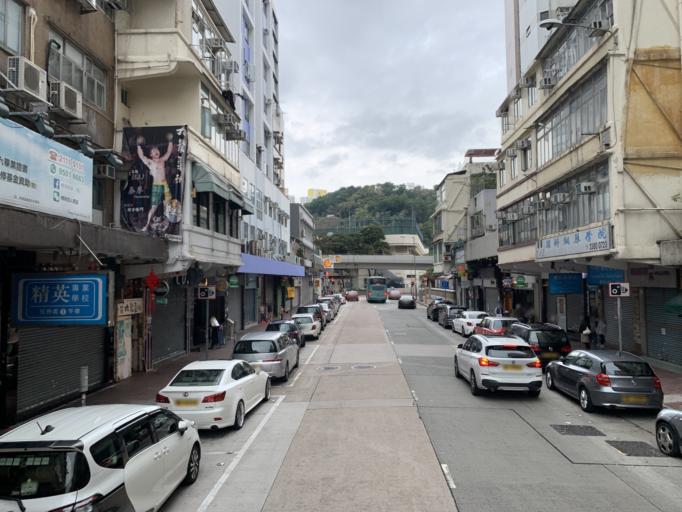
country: HK
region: Sham Shui Po
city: Sham Shui Po
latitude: 22.3256
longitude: 114.1692
